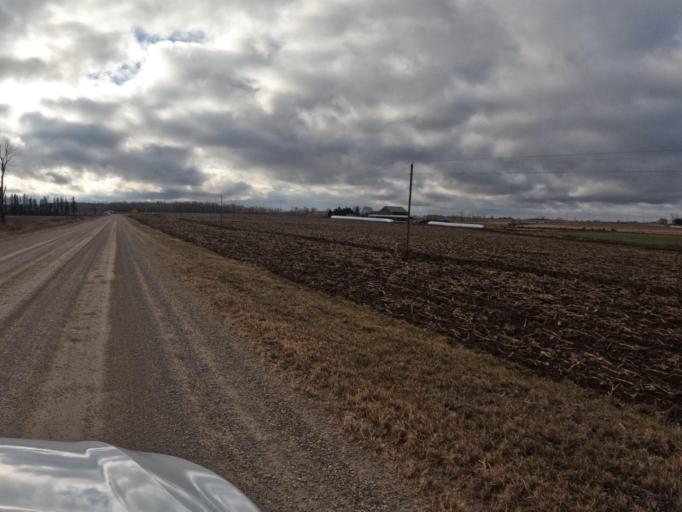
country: CA
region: Ontario
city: Shelburne
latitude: 43.8694
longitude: -80.3554
